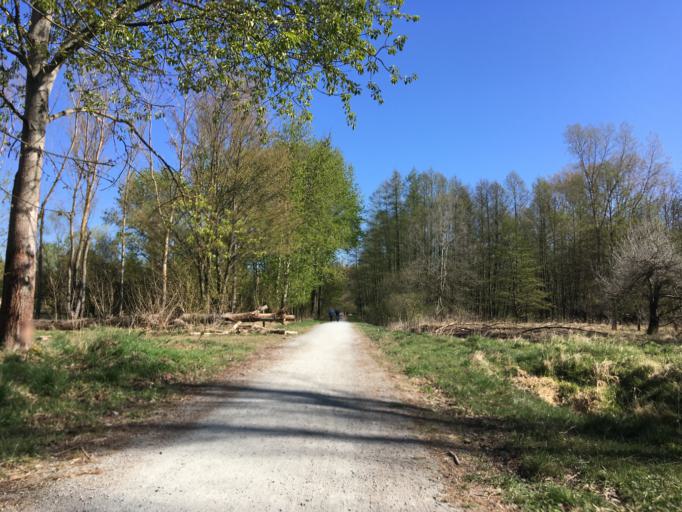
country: DE
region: Berlin
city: Buch
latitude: 52.6434
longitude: 13.4668
